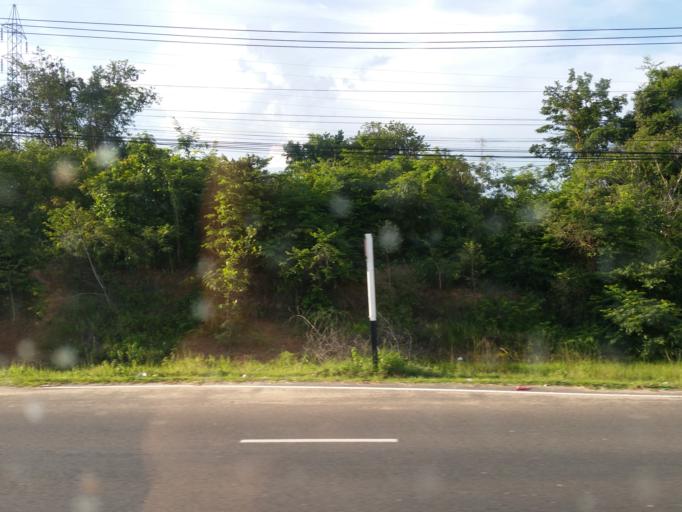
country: TH
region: Changwat Ubon Ratchathani
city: Sirindhorn
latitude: 15.2010
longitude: 105.3806
